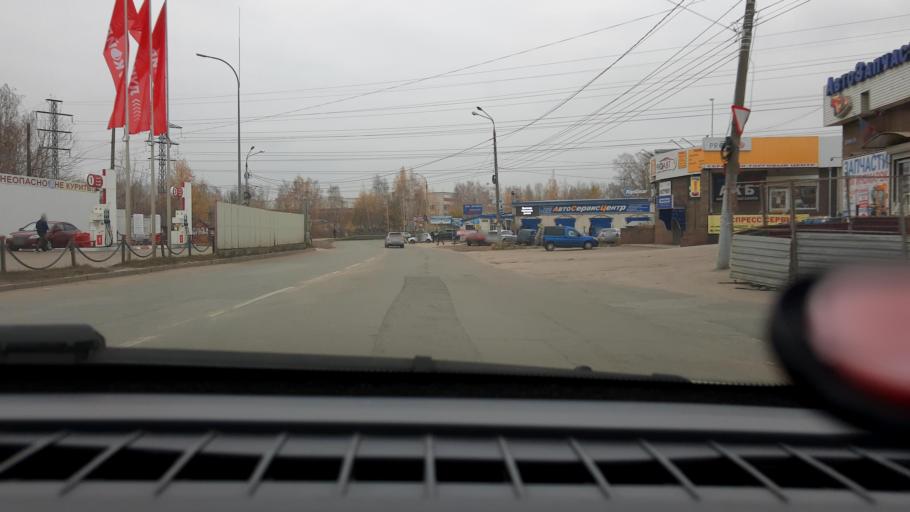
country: RU
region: Nizjnij Novgorod
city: Gorbatovka
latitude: 56.3580
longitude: 43.8055
